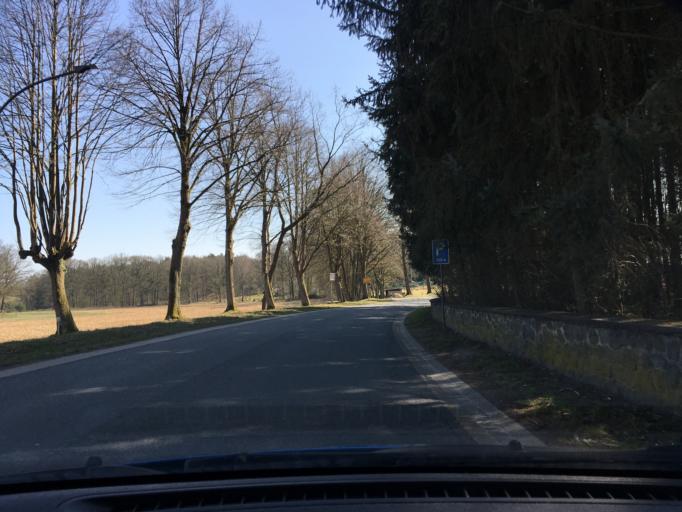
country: DE
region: Lower Saxony
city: Wriedel
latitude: 53.0730
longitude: 10.2843
